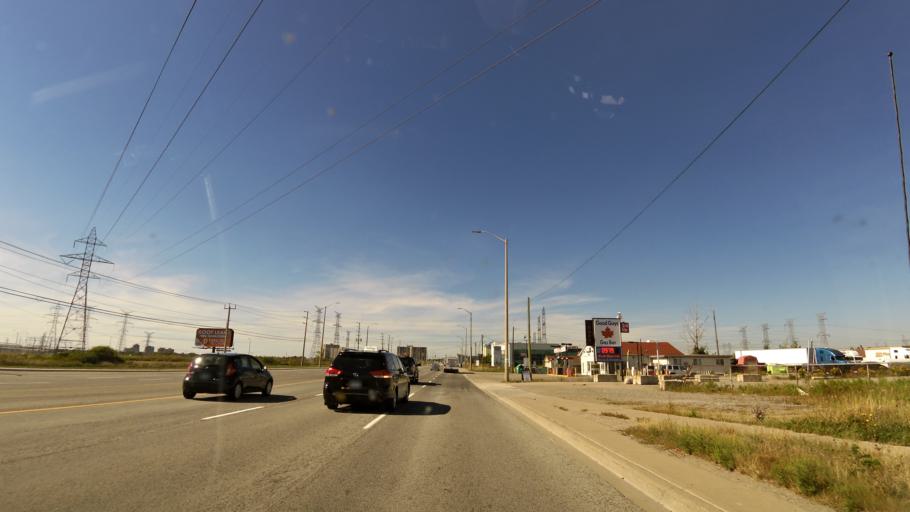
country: CA
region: Ontario
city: Brampton
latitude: 43.6485
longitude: -79.7094
